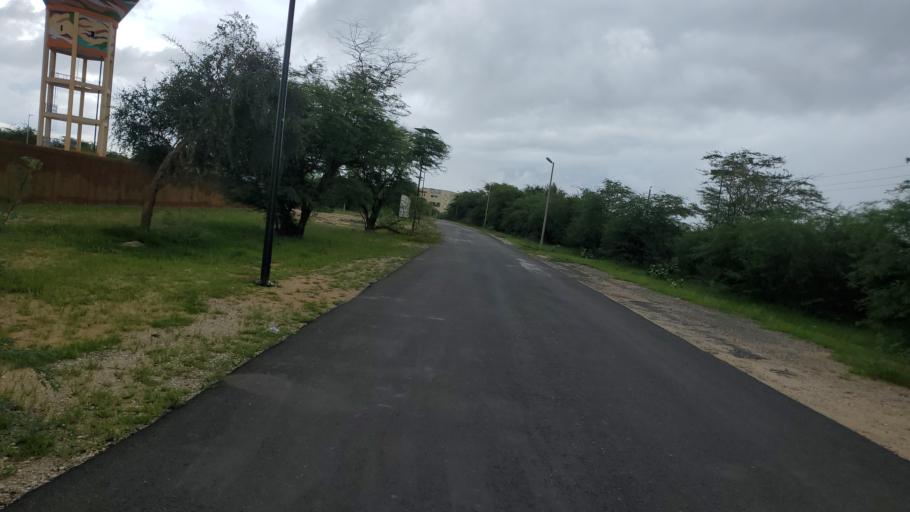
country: SN
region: Saint-Louis
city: Saint-Louis
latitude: 16.0590
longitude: -16.4280
